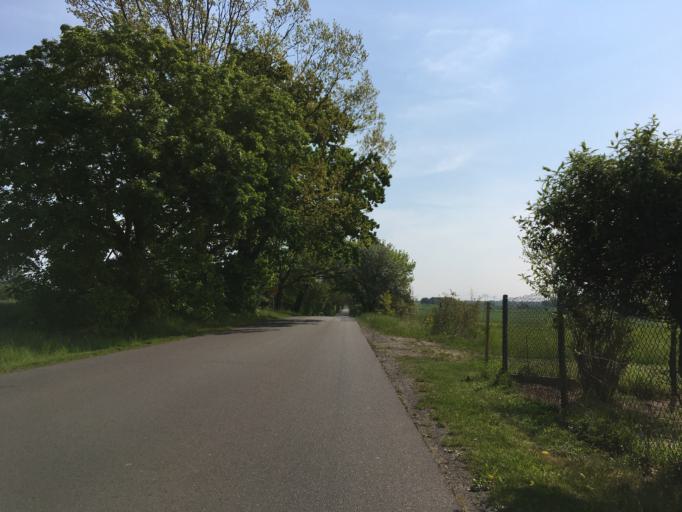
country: DE
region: Brandenburg
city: Neuenhagen
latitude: 52.5689
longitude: 13.6674
